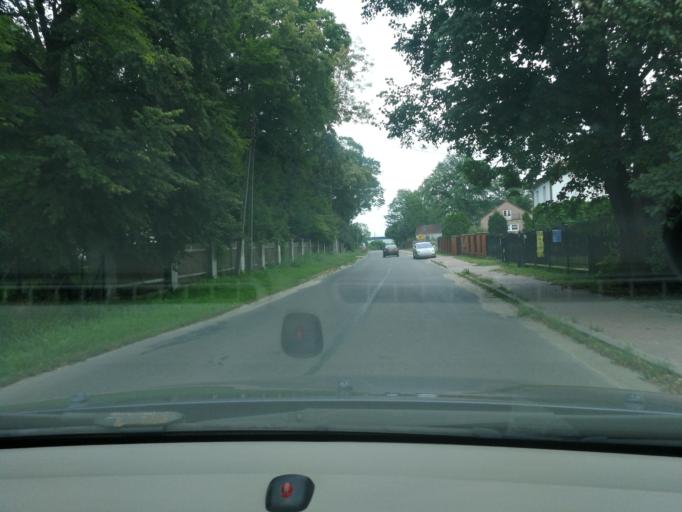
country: PL
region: Masovian Voivodeship
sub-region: Powiat grodziski
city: Grodzisk Mazowiecki
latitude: 52.1307
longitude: 20.5930
